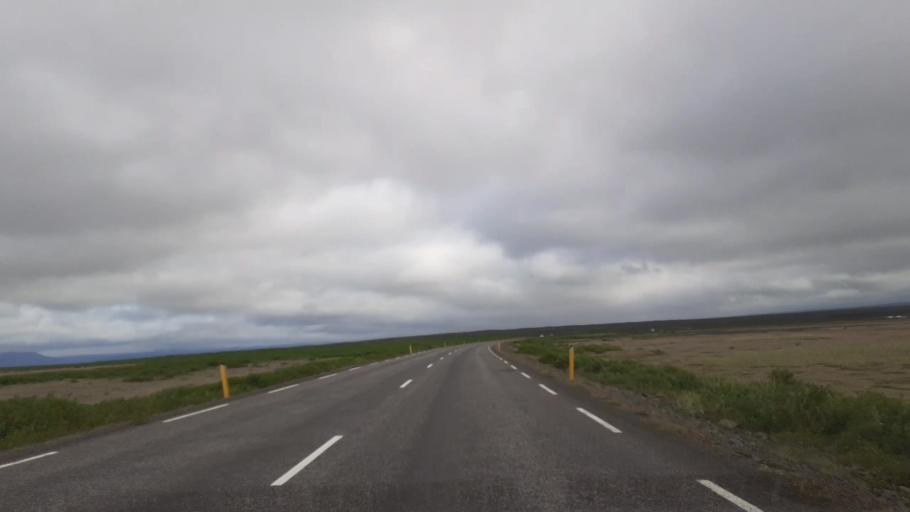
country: IS
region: Northeast
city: Husavik
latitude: 66.1161
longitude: -16.9126
